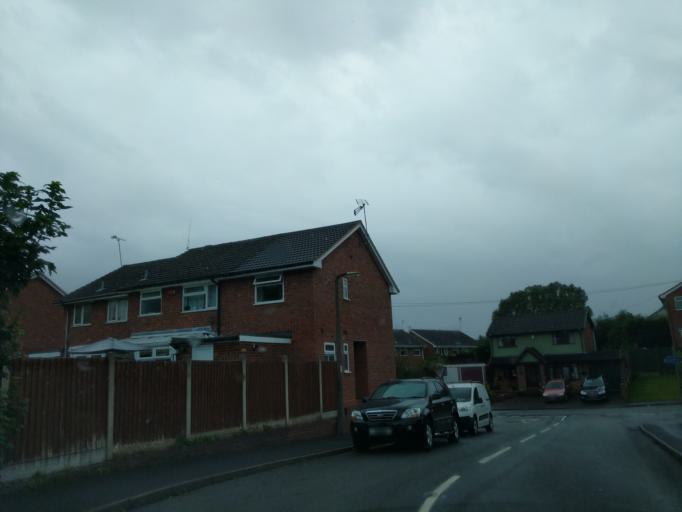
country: GB
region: England
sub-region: Staffordshire
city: Stafford
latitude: 52.8067
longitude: -2.0854
